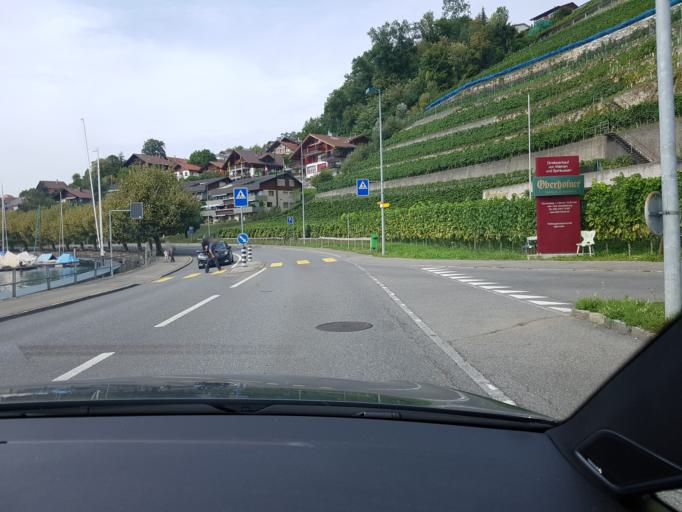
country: CH
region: Bern
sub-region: Thun District
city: Hilterfingen
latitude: 46.7273
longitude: 7.6771
